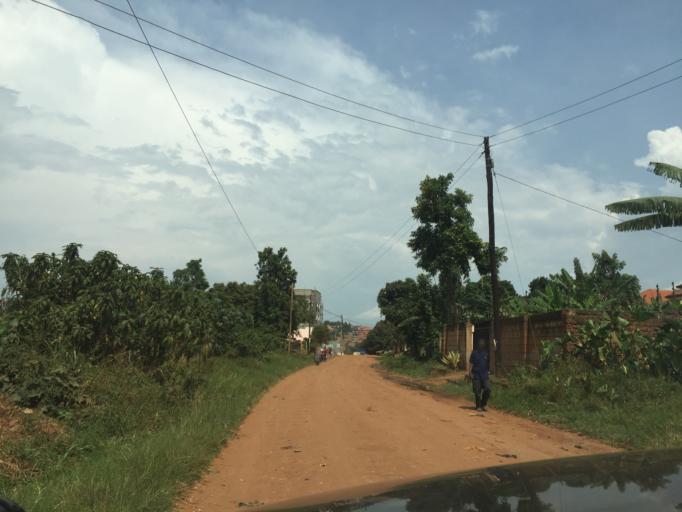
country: UG
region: Central Region
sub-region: Wakiso District
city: Kireka
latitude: 0.4135
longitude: 32.6221
